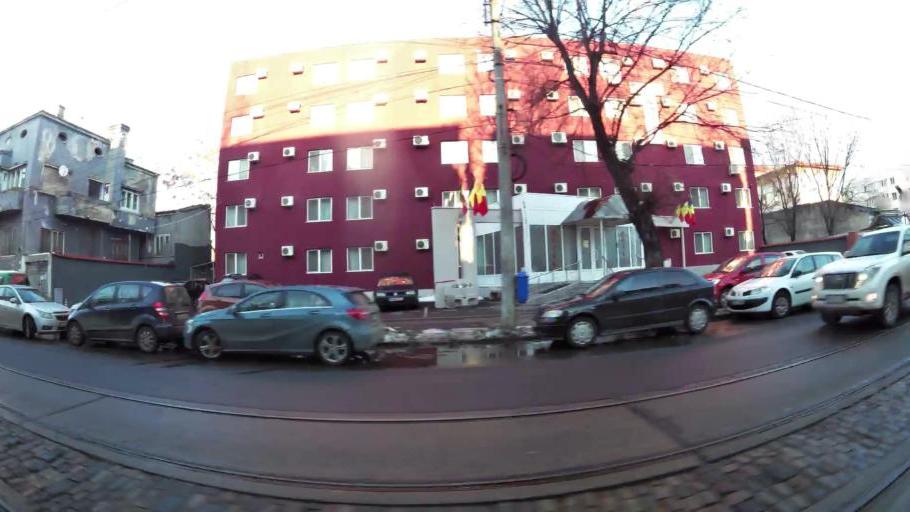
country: RO
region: Bucuresti
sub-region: Municipiul Bucuresti
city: Bucharest
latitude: 44.4469
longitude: 26.1338
